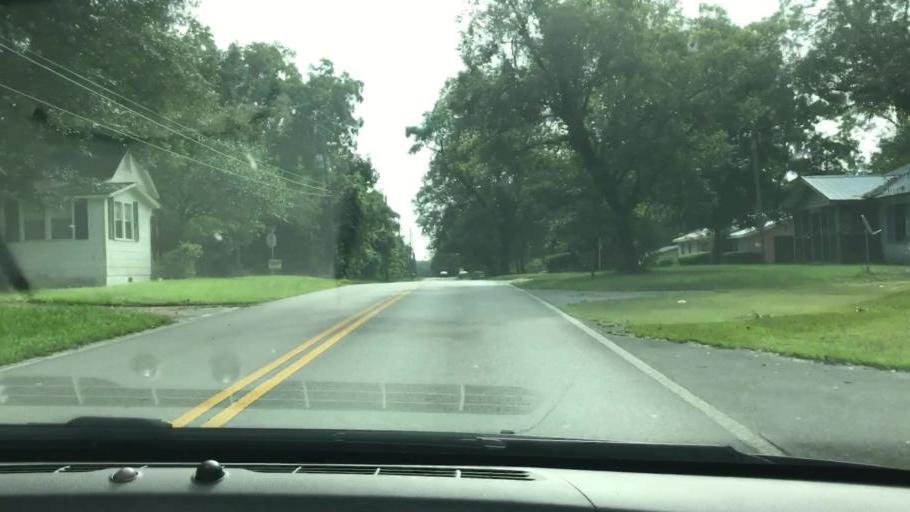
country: US
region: Florida
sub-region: Jackson County
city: Marianna
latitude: 30.7688
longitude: -85.2339
